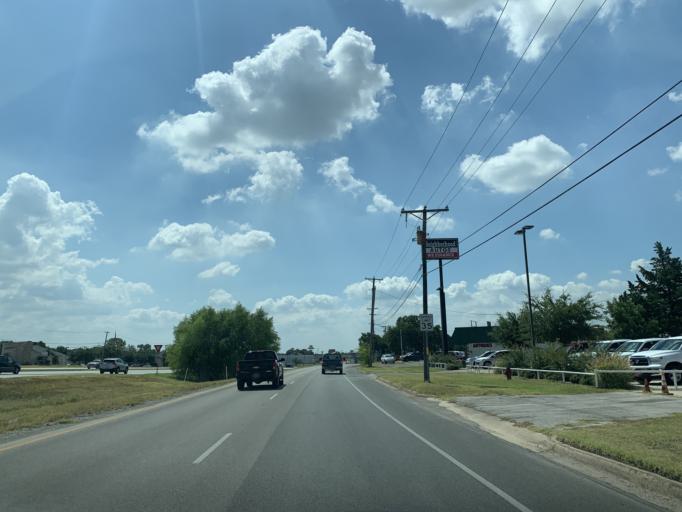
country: US
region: Texas
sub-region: Tarrant County
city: Azle
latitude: 32.8977
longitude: -97.5433
